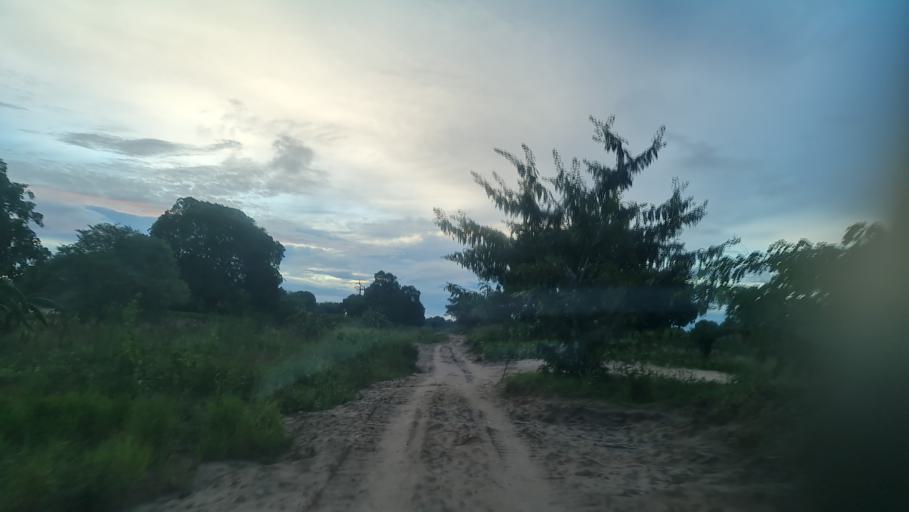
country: MZ
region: Nampula
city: Nampula
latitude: -14.7372
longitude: 39.9266
